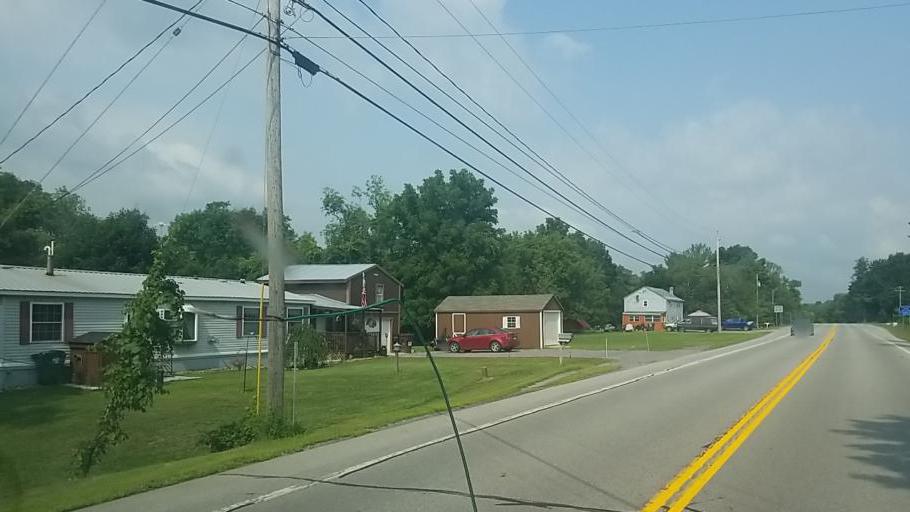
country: US
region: New York
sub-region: Montgomery County
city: Saint Johnsville
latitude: 42.9797
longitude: -74.6401
